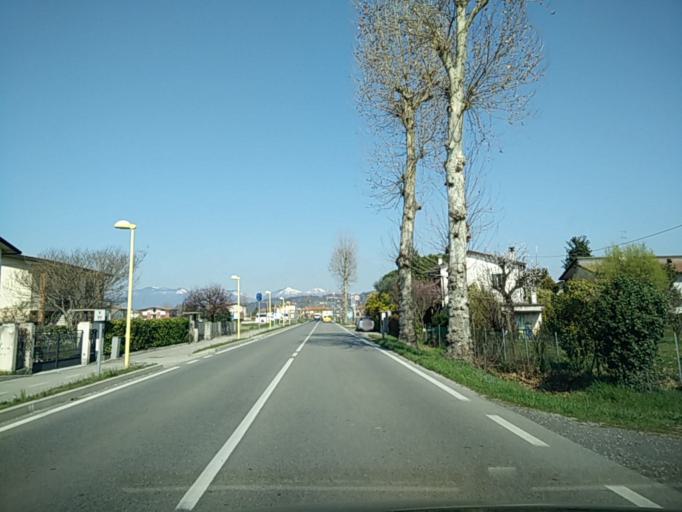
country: IT
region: Veneto
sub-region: Provincia di Treviso
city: Nervesa della Battaglia
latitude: 45.8194
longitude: 12.2238
